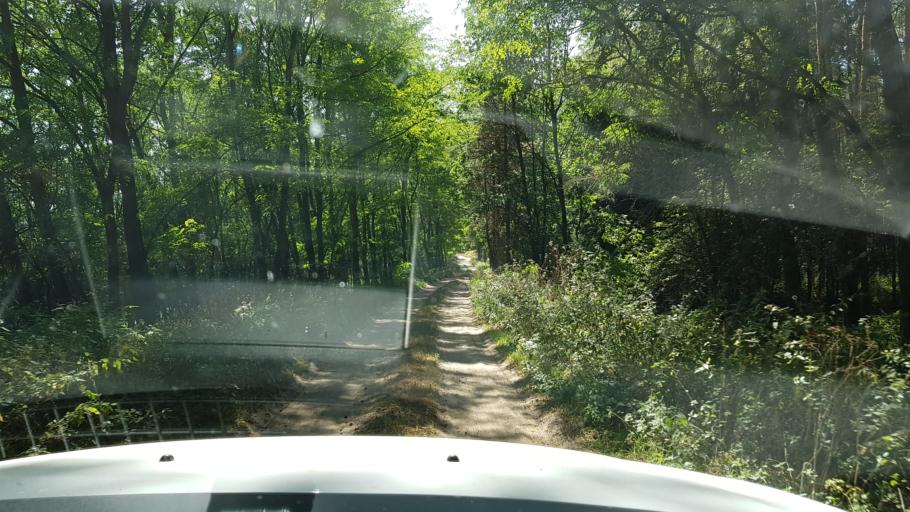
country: PL
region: West Pomeranian Voivodeship
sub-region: Powiat gryfinski
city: Cedynia
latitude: 52.8391
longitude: 14.2552
